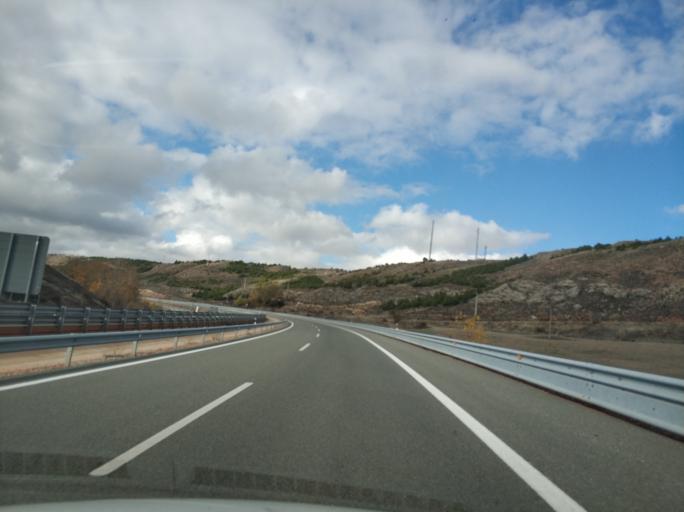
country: ES
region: Castille and Leon
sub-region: Provincia de Soria
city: Medinaceli
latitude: 41.1906
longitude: -2.4321
